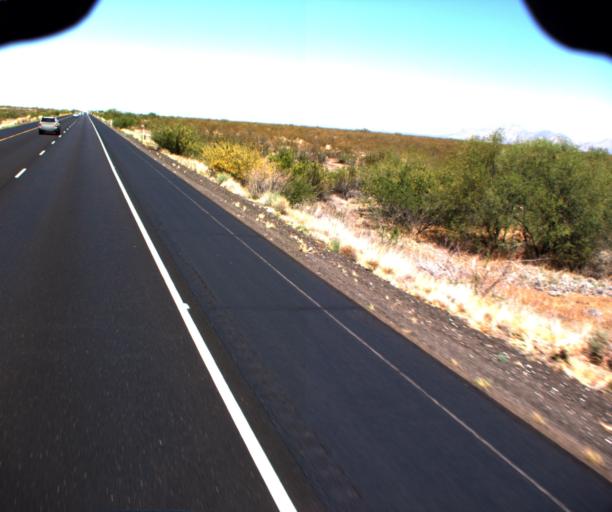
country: US
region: Arizona
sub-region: Yavapai County
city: Congress
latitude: 34.0743
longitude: -112.8800
